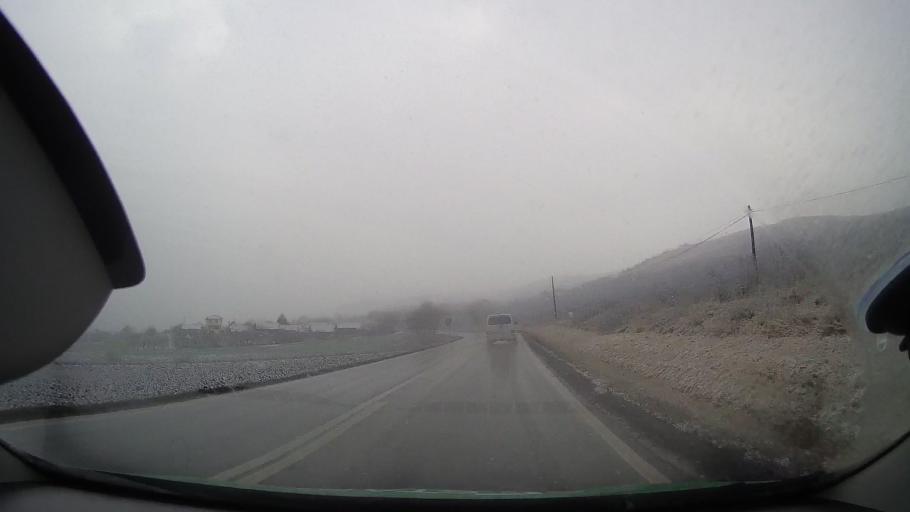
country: RO
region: Mures
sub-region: Municipiul Tarnaveni
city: Tarnaveni
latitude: 46.2868
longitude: 24.3017
